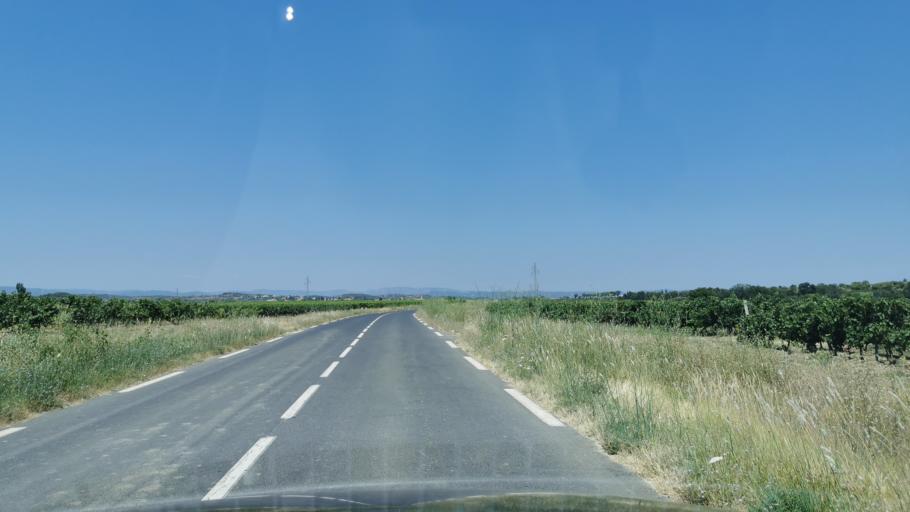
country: FR
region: Languedoc-Roussillon
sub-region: Departement de l'Herault
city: Maureilhan
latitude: 43.3684
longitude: 3.1147
